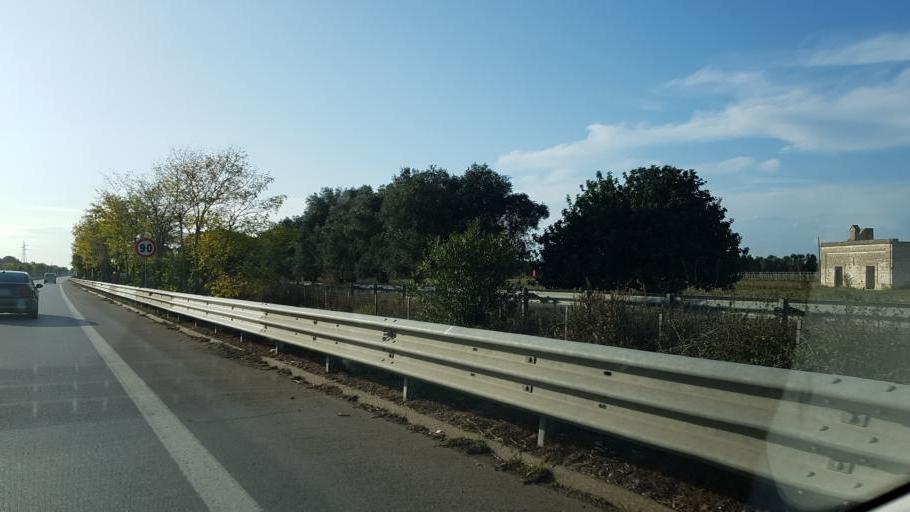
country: IT
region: Apulia
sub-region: Provincia di Brindisi
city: Oria
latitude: 40.5359
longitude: 17.6408
